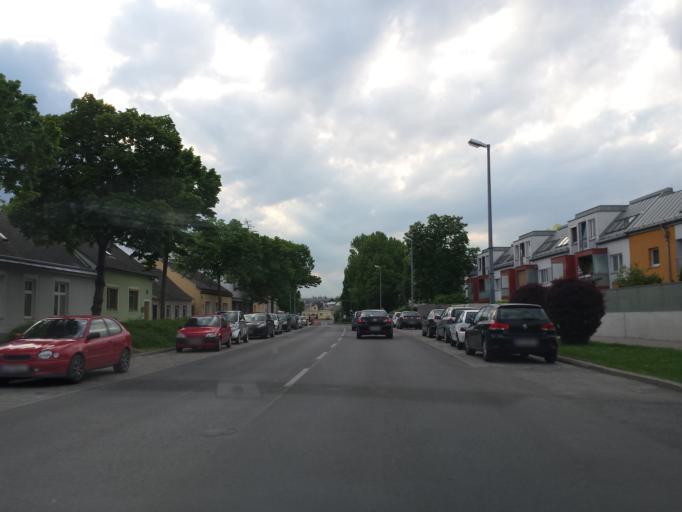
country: AT
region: Lower Austria
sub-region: Politischer Bezirk Ganserndorf
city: Gross-Enzersdorf
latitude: 48.2134
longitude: 16.5282
